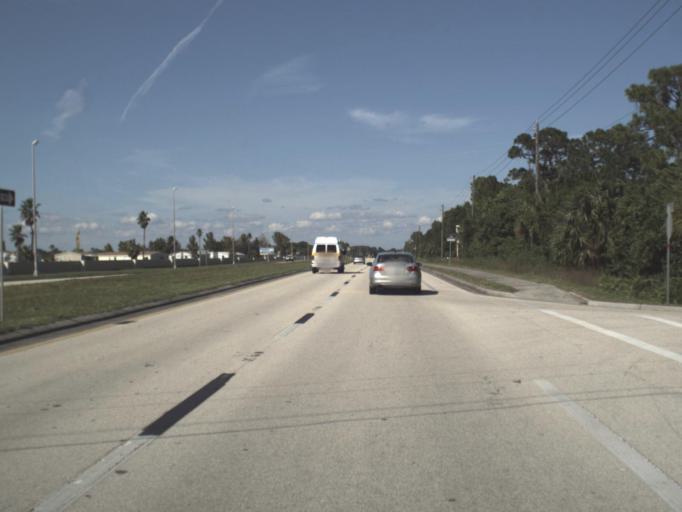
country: US
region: Florida
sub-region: Sarasota County
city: North Port
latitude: 26.9733
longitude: -82.2089
